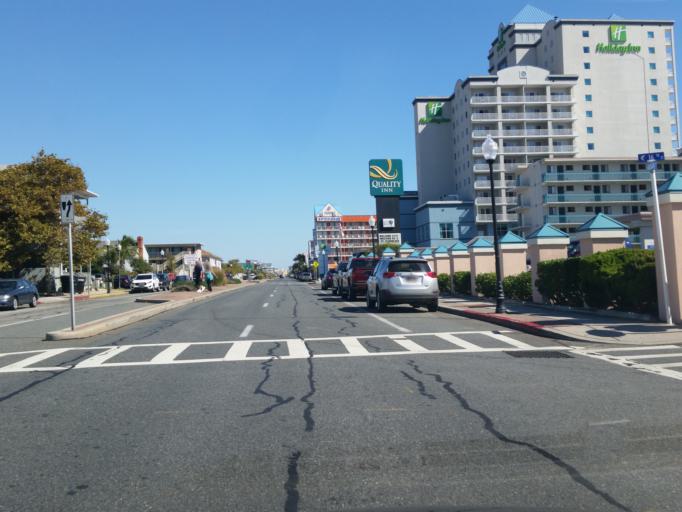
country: US
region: Maryland
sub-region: Worcester County
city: Ocean City
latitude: 38.3457
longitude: -75.0786
